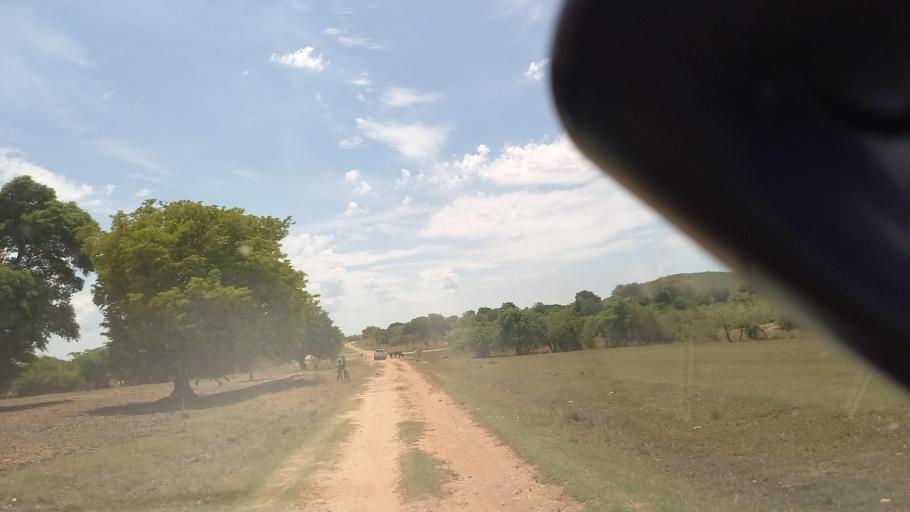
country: ZM
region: Southern
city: Mazabuka
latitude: -16.1387
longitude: 27.7589
